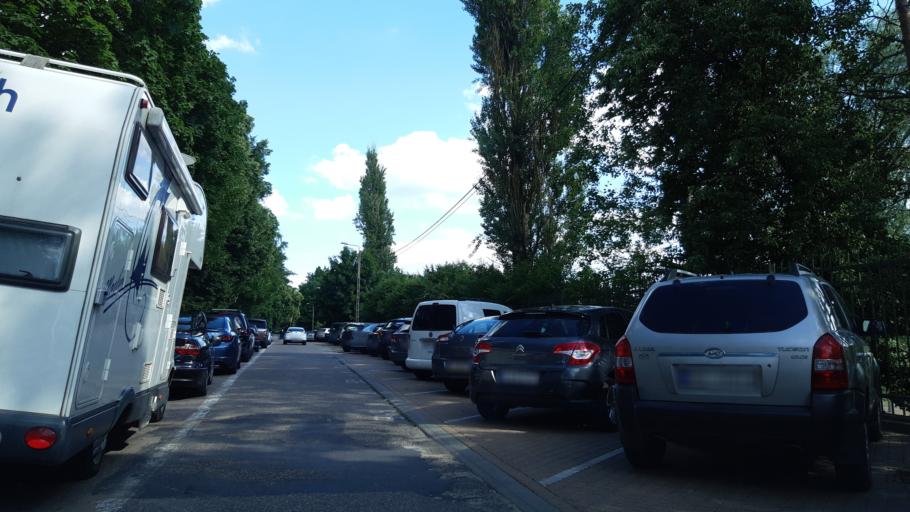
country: PL
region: Warmian-Masurian Voivodeship
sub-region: Powiat mragowski
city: Mragowo
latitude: 53.8756
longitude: 21.3171
